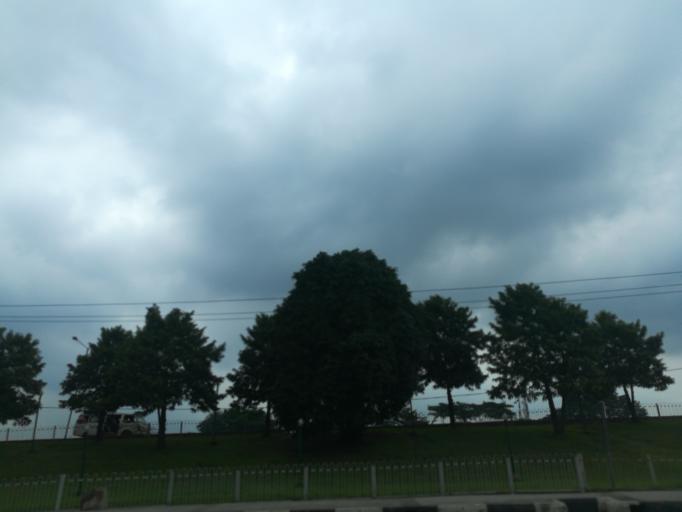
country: NG
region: Lagos
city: Ikeja
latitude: 6.6190
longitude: 3.3643
